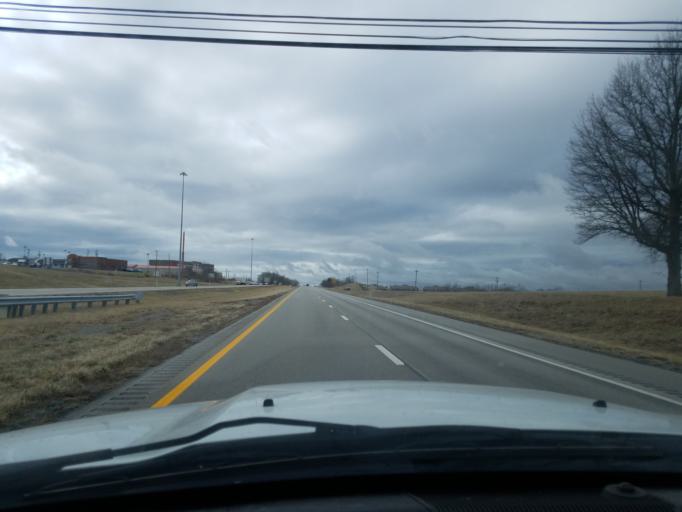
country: US
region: Kentucky
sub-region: Montgomery County
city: Mount Sterling
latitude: 38.0780
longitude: -83.9495
